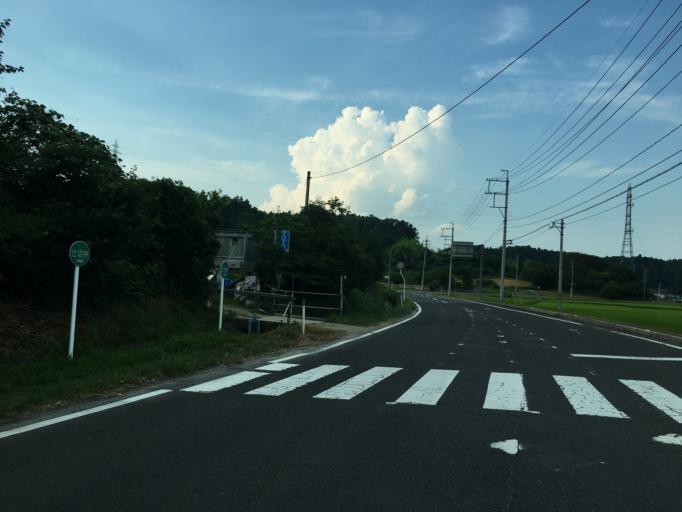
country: JP
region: Fukushima
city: Nihommatsu
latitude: 37.5651
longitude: 140.4335
